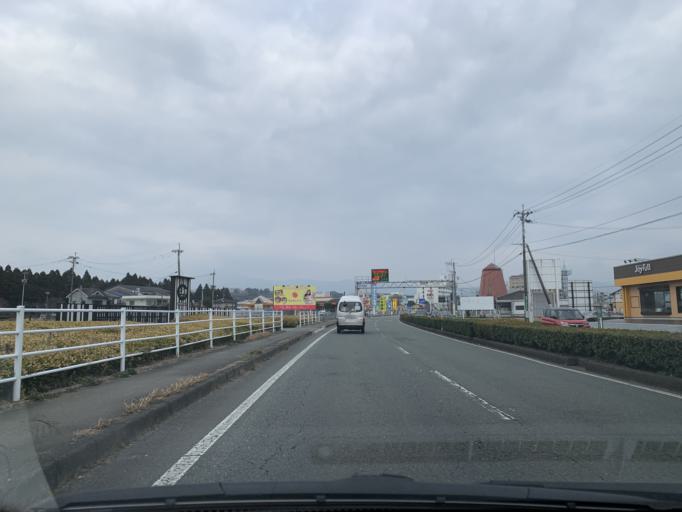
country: JP
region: Kumamoto
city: Ozu
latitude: 32.8744
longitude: 130.8487
